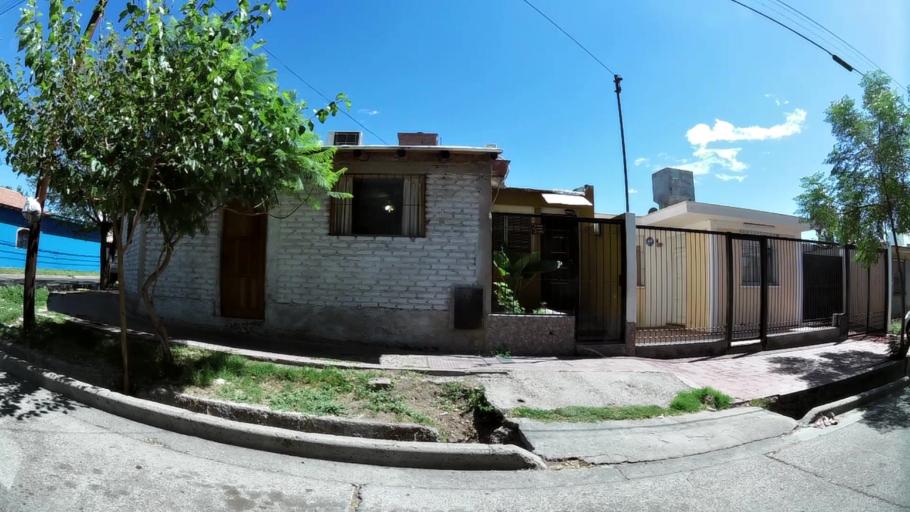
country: AR
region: Mendoza
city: Las Heras
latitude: -32.8565
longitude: -68.8656
